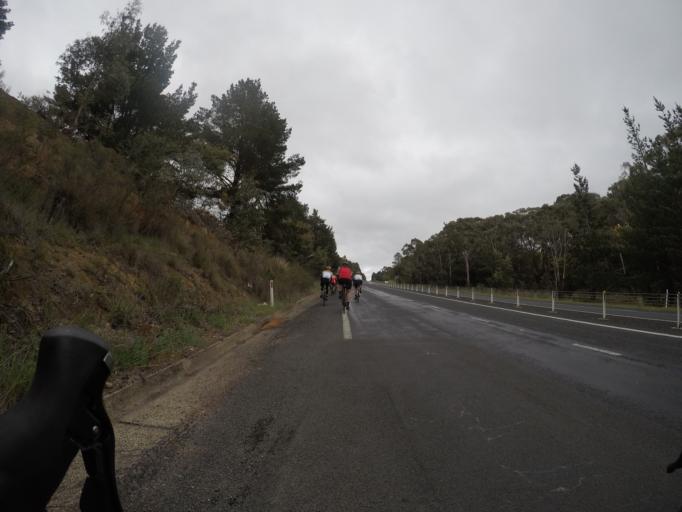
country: AU
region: New South Wales
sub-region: Lithgow
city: Portland
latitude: -33.4338
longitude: 149.8747
